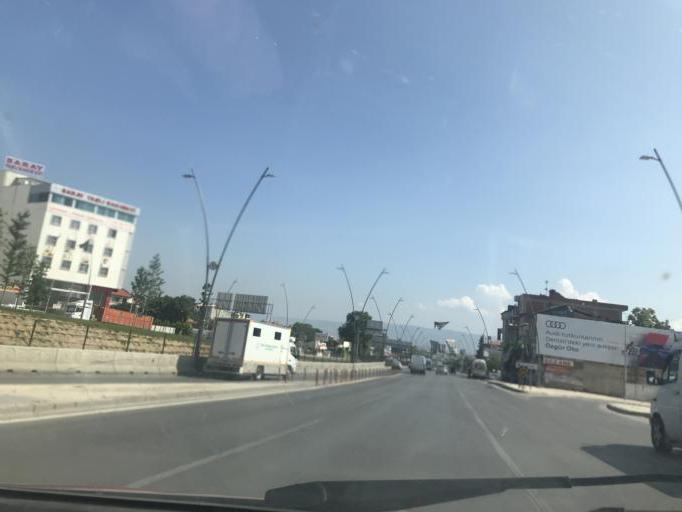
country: TR
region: Denizli
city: Denizli
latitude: 37.7837
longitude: 29.0978
